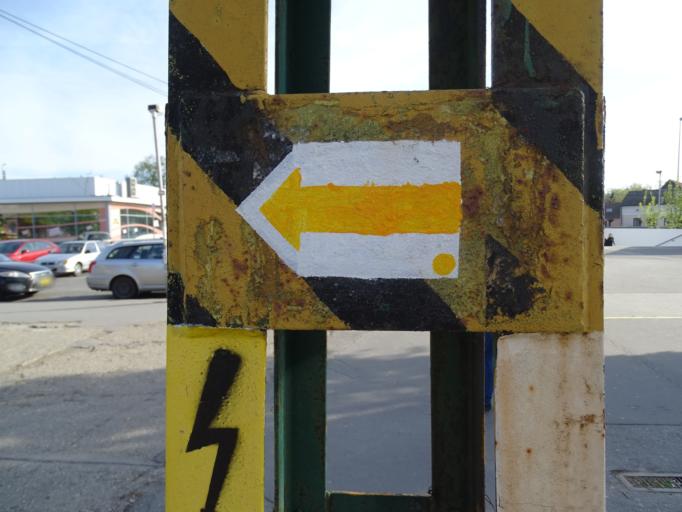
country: HU
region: Pest
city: Szentendre
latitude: 47.6613
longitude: 19.0757
